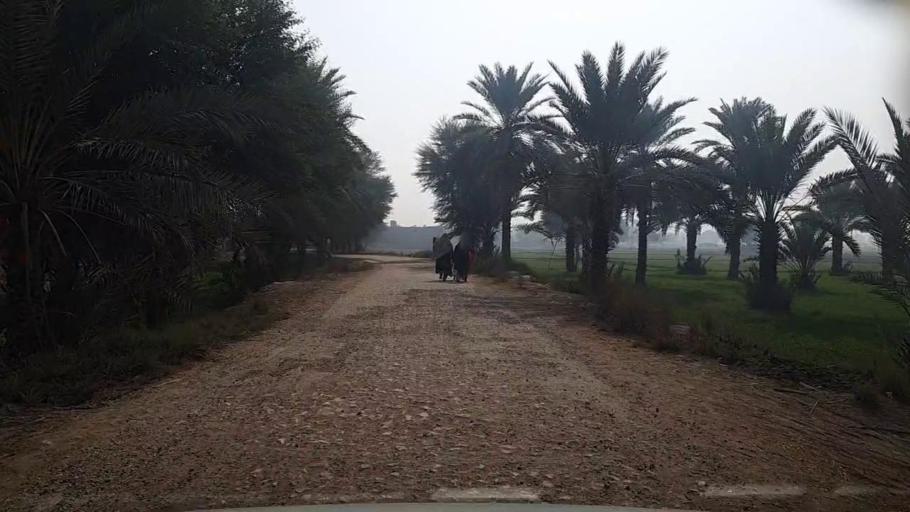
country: PK
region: Sindh
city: Setharja Old
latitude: 27.1568
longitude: 68.4630
